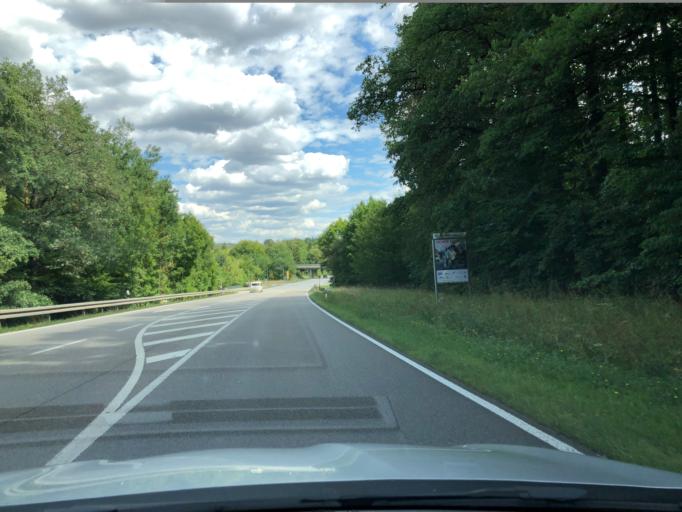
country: DE
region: Bavaria
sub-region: Upper Palatinate
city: Sulzbach-Rosenberg
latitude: 49.4966
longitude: 11.7266
